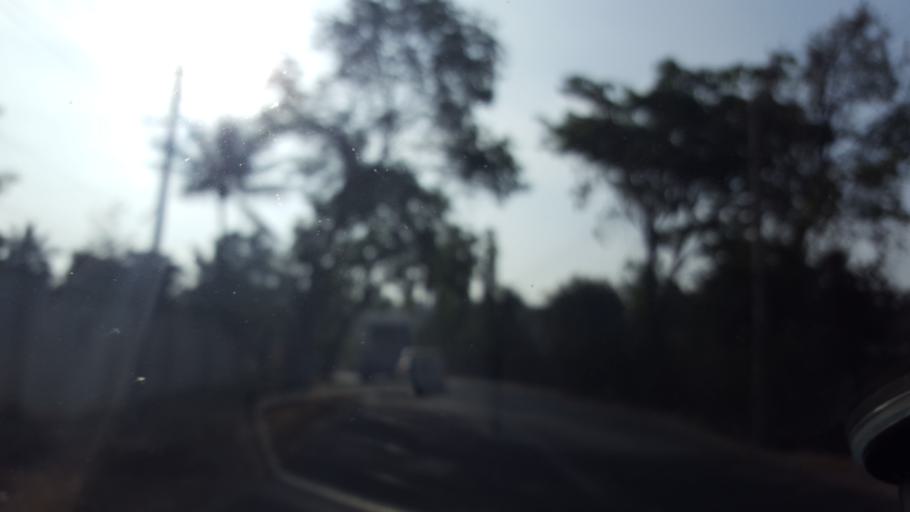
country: IN
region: Karnataka
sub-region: Bangalore Urban
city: Bangalore
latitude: 12.9053
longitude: 77.5029
